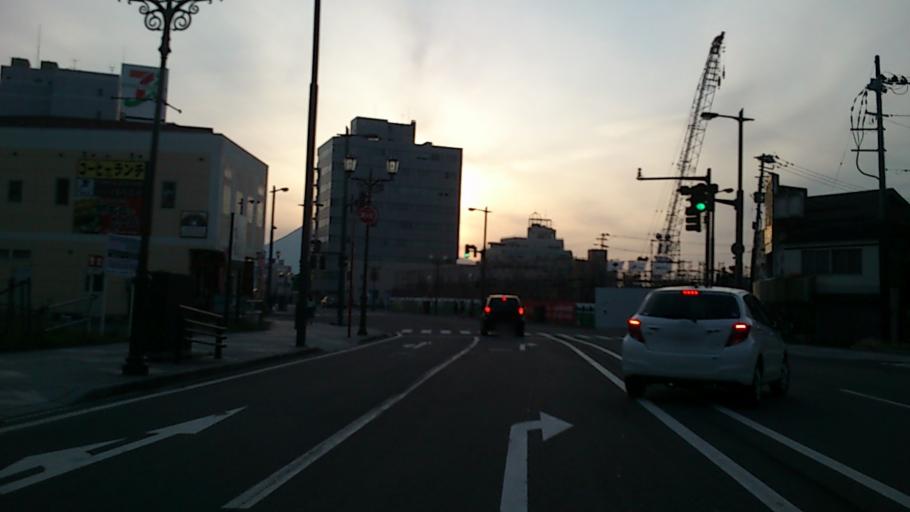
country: JP
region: Aomori
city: Hirosaki
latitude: 40.5995
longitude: 140.4834
